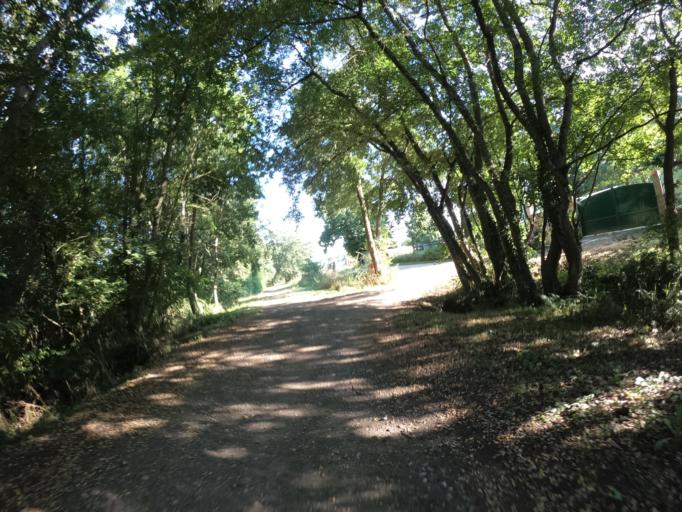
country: FR
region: Midi-Pyrenees
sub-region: Departement de l'Ariege
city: La Tour-du-Crieu
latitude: 43.1126
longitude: 1.7204
